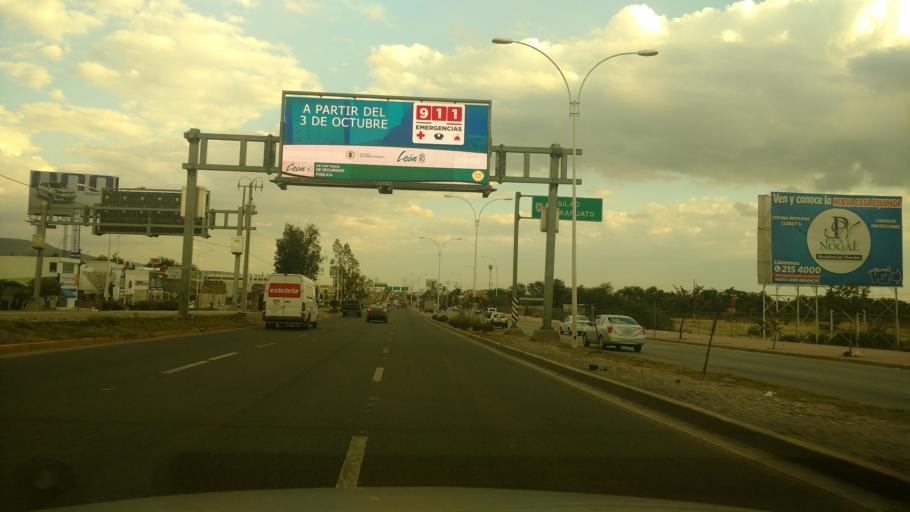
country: MX
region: Guanajuato
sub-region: Leon
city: Medina
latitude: 21.1674
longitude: -101.6535
